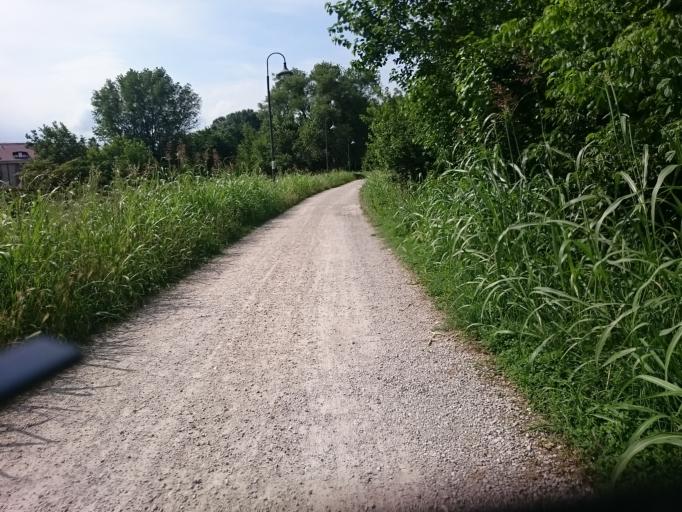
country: IT
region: Veneto
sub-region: Provincia di Padova
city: Padova
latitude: 45.4029
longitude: 11.9151
